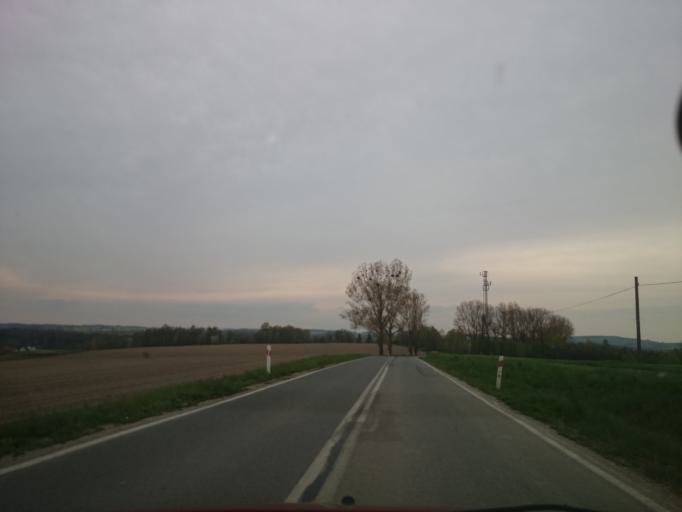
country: PL
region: Lower Silesian Voivodeship
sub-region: Powiat strzelinski
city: Przeworno
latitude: 50.6427
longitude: 17.1833
